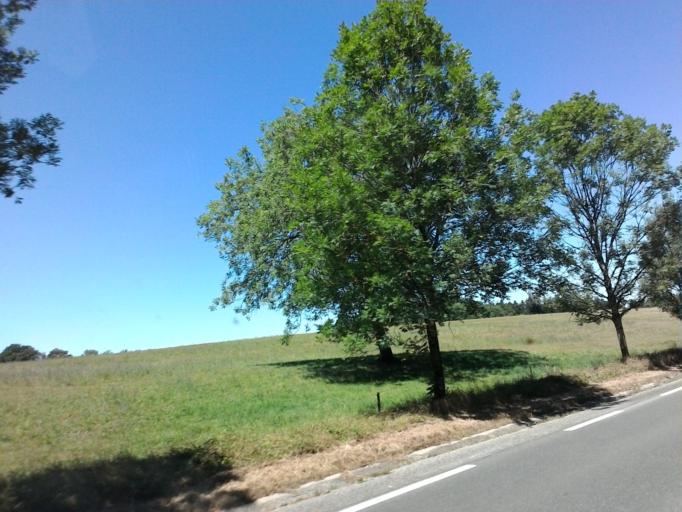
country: FR
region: Bourgogne
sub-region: Departement de Saone-et-Loire
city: Cuiseaux
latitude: 46.4769
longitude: 5.3627
